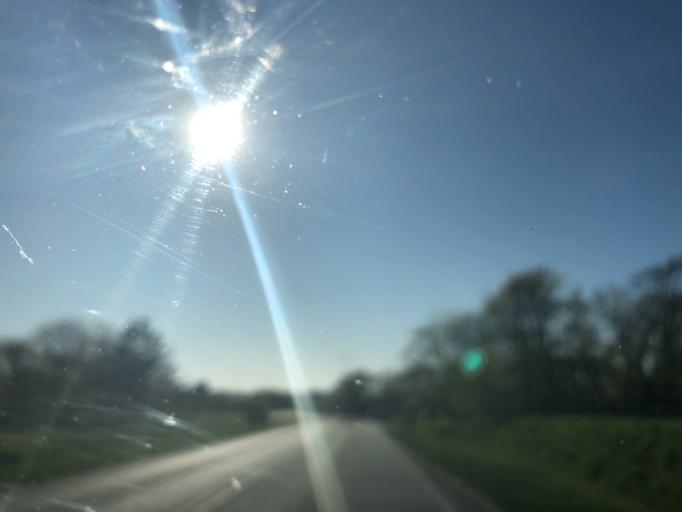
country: DK
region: Central Jutland
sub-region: Holstebro Kommune
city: Vinderup
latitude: 56.4679
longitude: 8.7733
